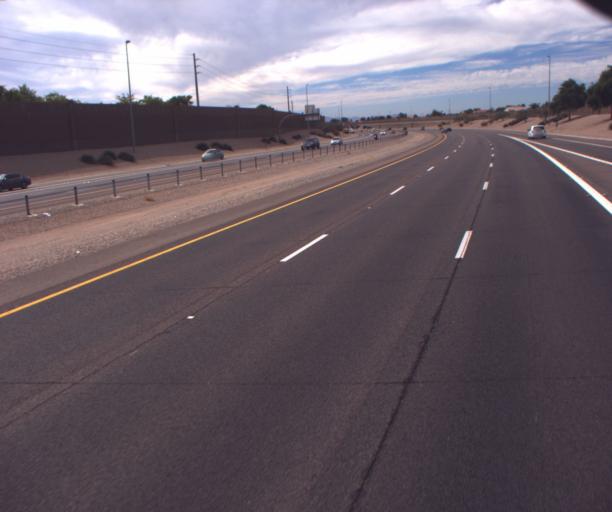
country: US
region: Arizona
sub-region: Maricopa County
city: Gilbert
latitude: 33.3280
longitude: -111.7264
